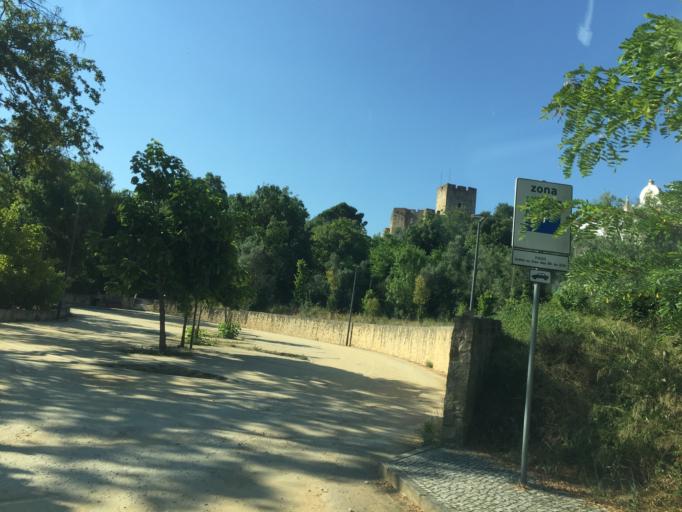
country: PT
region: Santarem
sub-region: Tomar
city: Tomar
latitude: 39.6052
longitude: -8.4178
